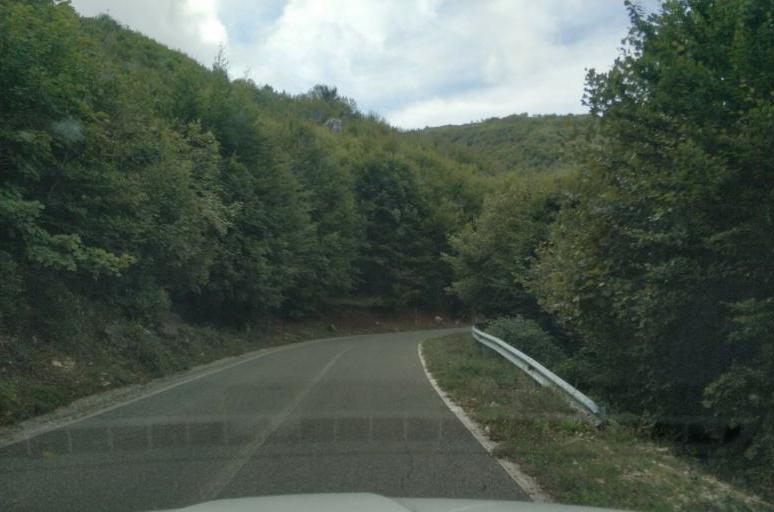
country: AL
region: Durres
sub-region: Rrethi i Krujes
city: Kruje
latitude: 41.5247
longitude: 19.8039
